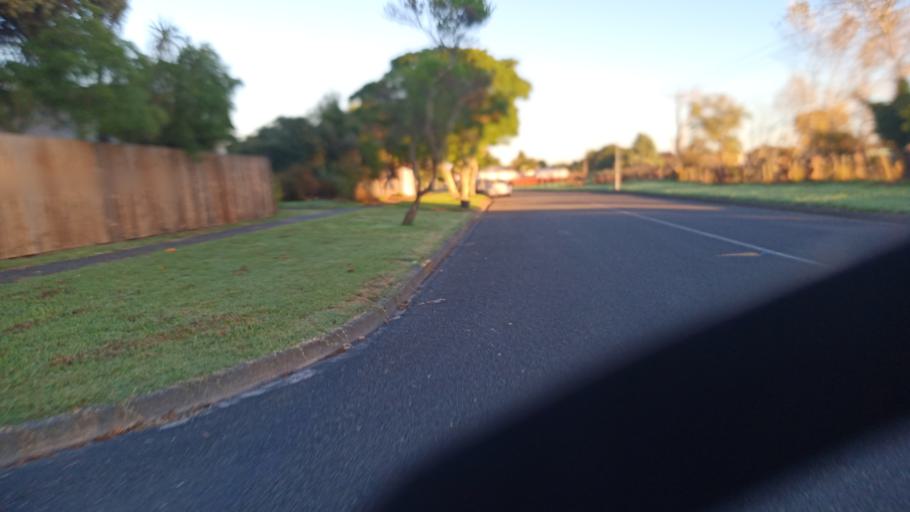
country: NZ
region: Gisborne
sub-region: Gisborne District
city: Gisborne
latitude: -38.6597
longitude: 177.9930
